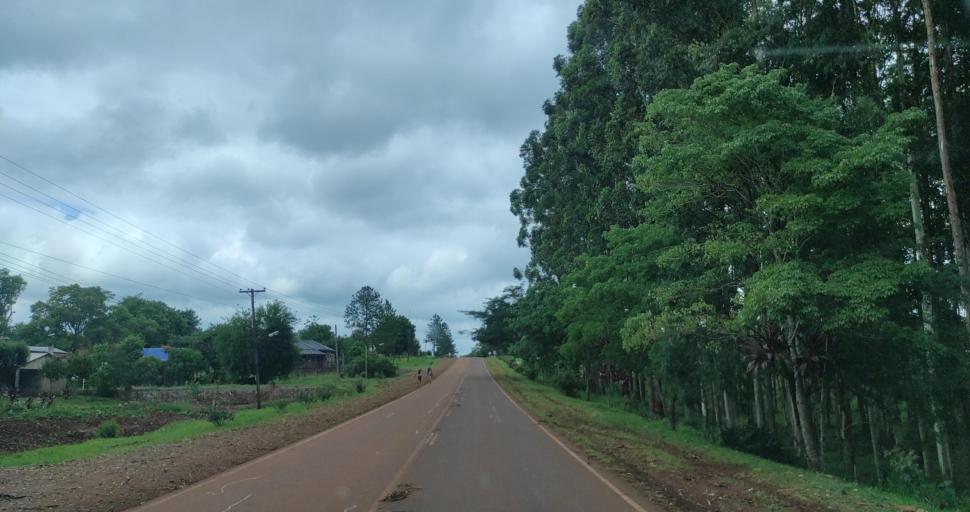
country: AR
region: Misiones
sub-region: Departamento de Veinticinco de Mayo
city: Veinticinco de Mayo
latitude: -27.3911
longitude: -54.7483
